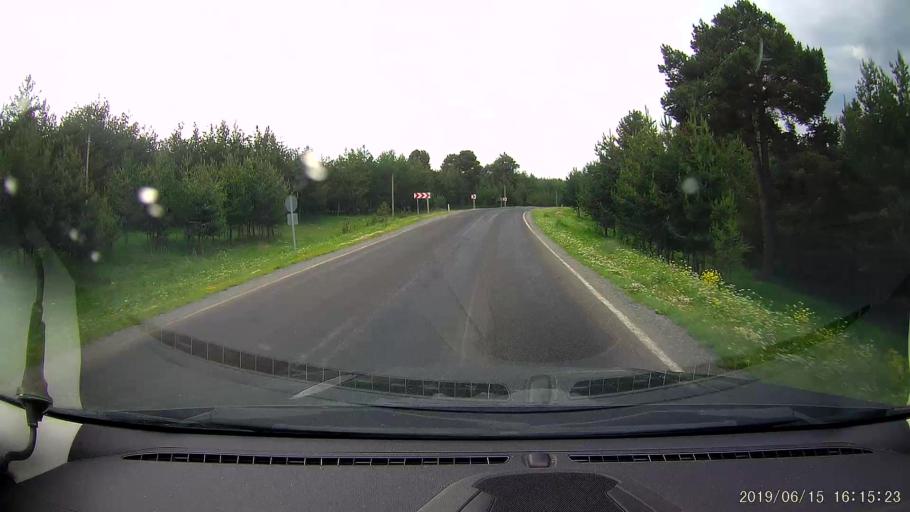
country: TR
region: Ardahan
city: Hanak
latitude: 41.2691
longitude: 42.8558
